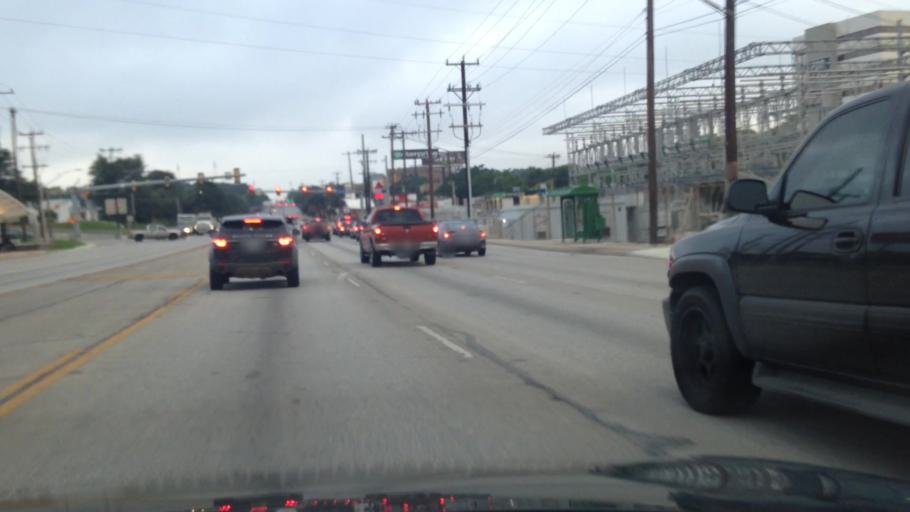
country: US
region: Texas
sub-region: Bexar County
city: Balcones Heights
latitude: 29.5021
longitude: -98.5597
